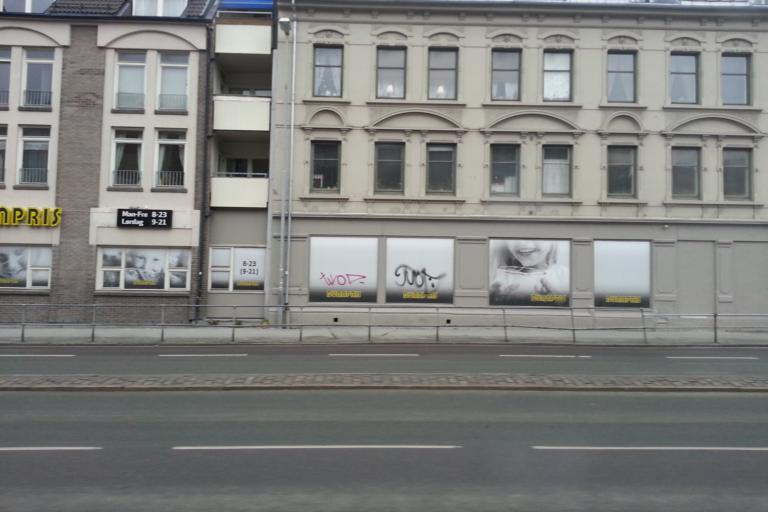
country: NO
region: Sor-Trondelag
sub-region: Trondheim
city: Trondheim
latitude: 63.4363
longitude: 10.4246
